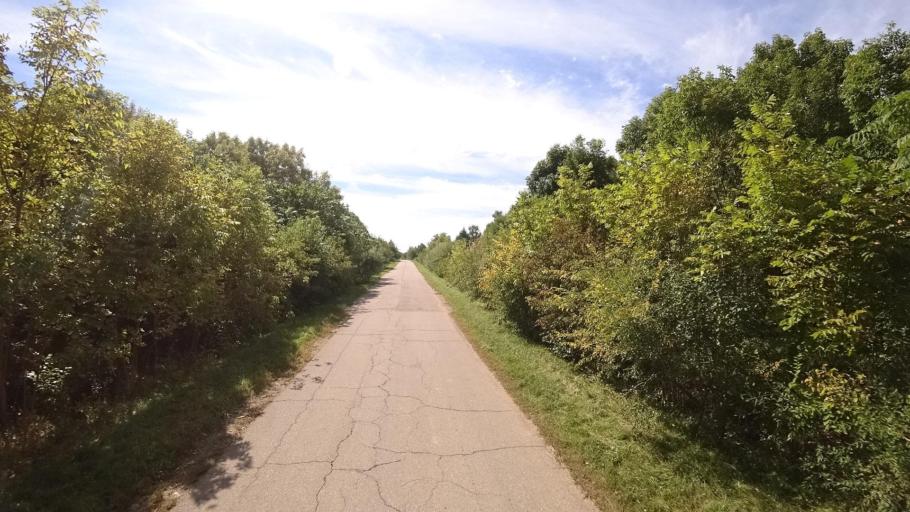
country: RU
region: Primorskiy
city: Kirovskiy
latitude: 44.7579
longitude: 133.6072
